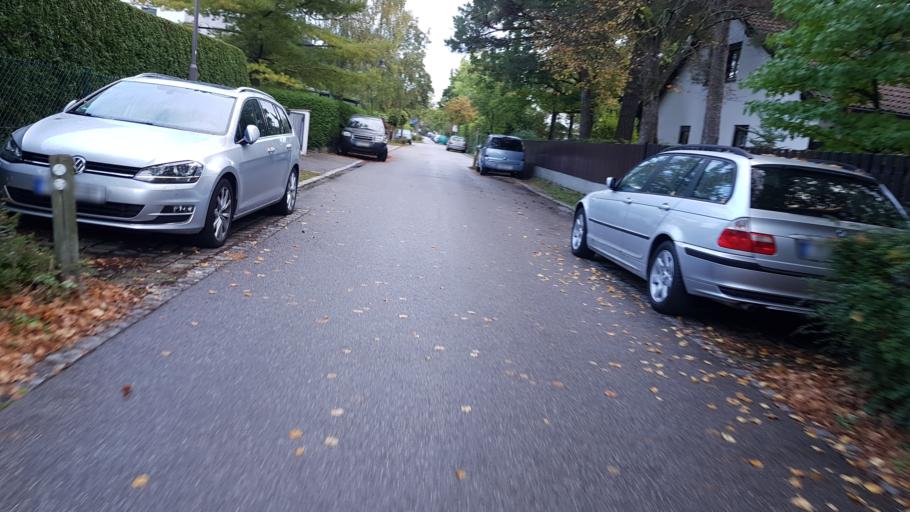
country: DE
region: Bavaria
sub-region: Upper Bavaria
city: Ottobrunn
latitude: 48.0760
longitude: 11.6736
